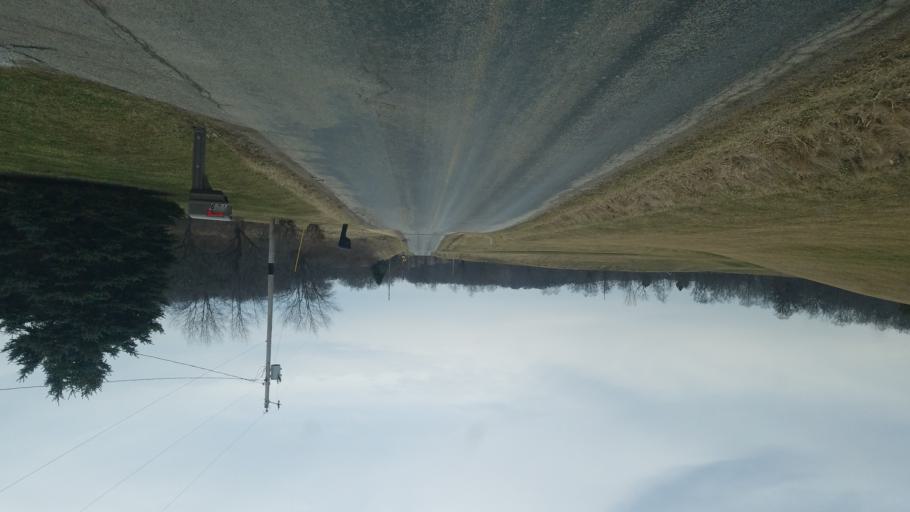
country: US
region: Ohio
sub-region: Richland County
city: Lincoln Heights
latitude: 40.7311
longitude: -82.3790
